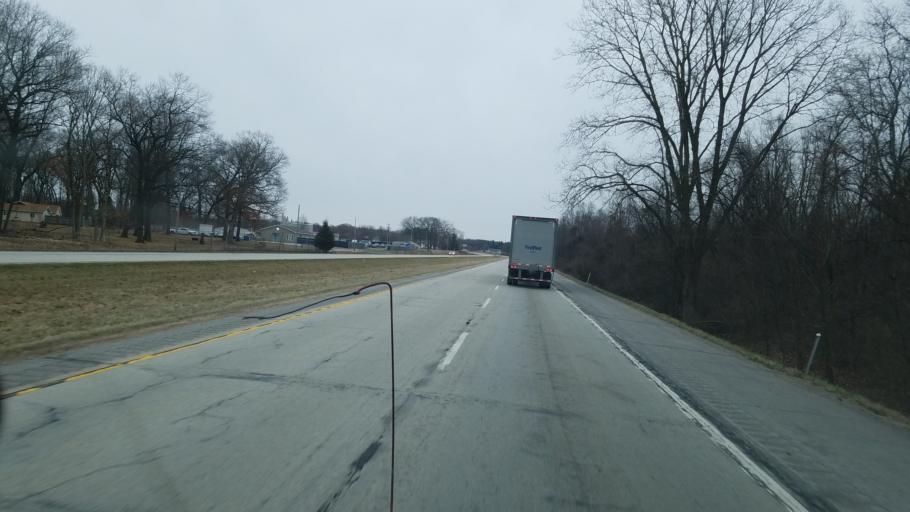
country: US
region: Indiana
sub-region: Starke County
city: Koontz Lake
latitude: 41.3659
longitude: -86.4748
